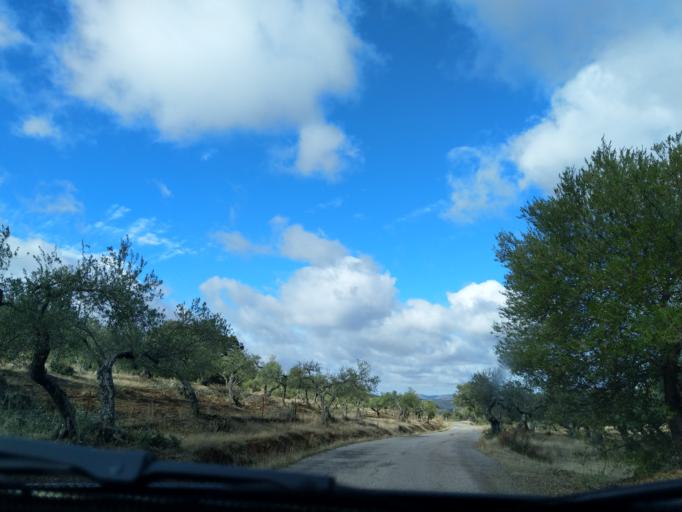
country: ES
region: Extremadura
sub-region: Provincia de Badajoz
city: Reina
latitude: 38.1293
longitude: -5.9355
